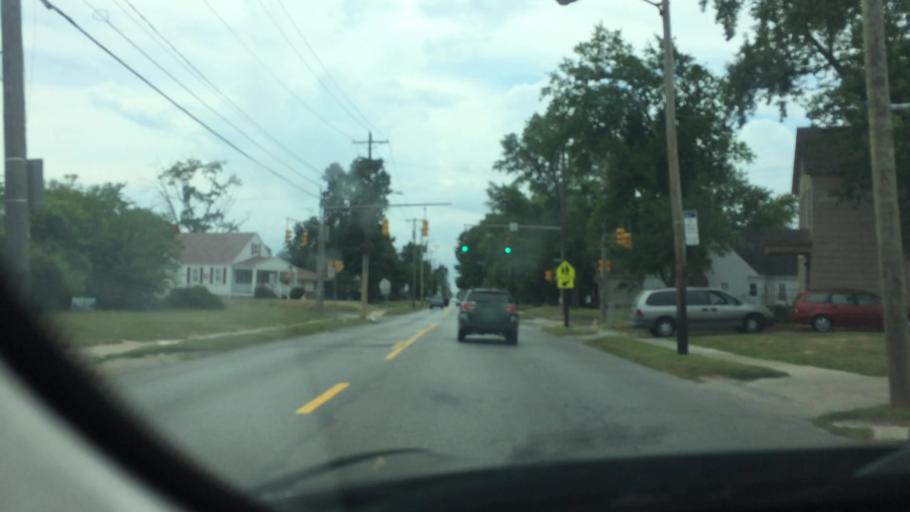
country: US
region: Ohio
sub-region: Wood County
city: Rossford
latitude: 41.6299
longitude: -83.6025
